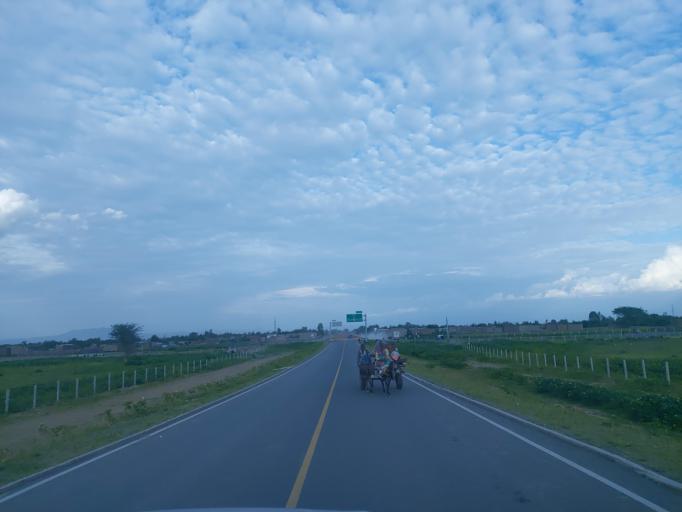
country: ET
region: Oromiya
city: Ziway
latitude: 8.1477
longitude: 38.7989
